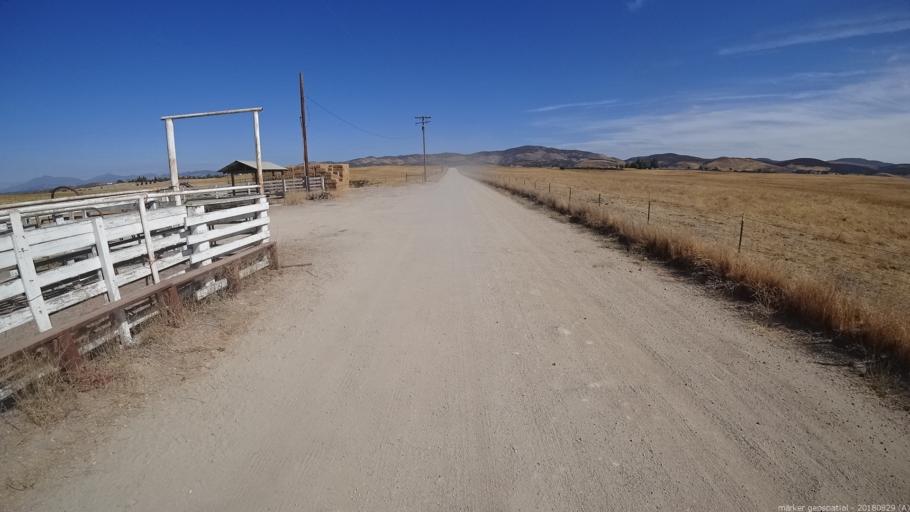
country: US
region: California
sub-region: Monterey County
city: King City
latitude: 35.9522
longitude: -121.0999
